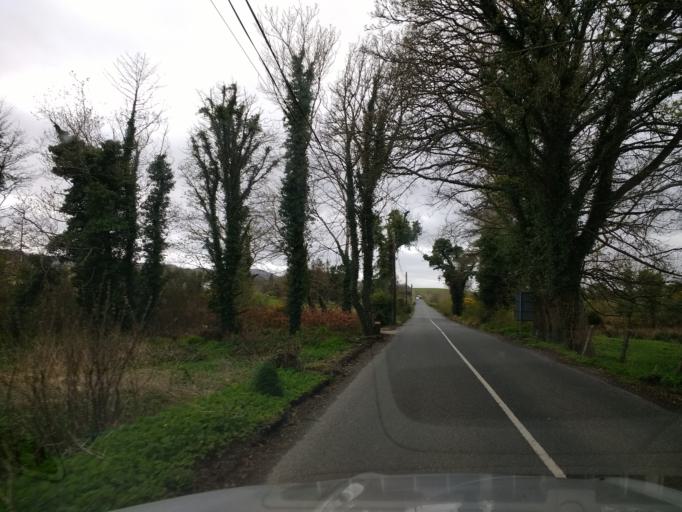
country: IE
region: Ulster
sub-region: County Donegal
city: Ramelton
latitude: 55.2047
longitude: -7.6368
